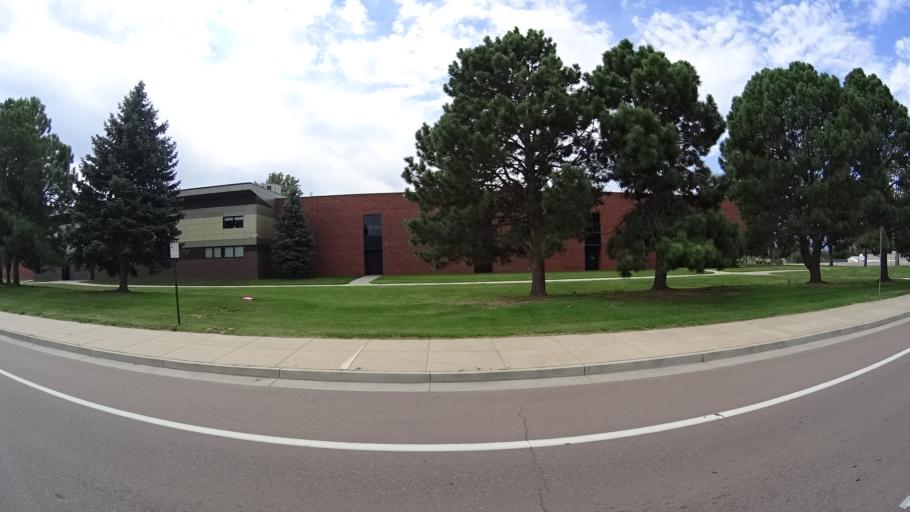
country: US
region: Colorado
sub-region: El Paso County
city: Cimarron Hills
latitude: 38.8969
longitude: -104.7444
